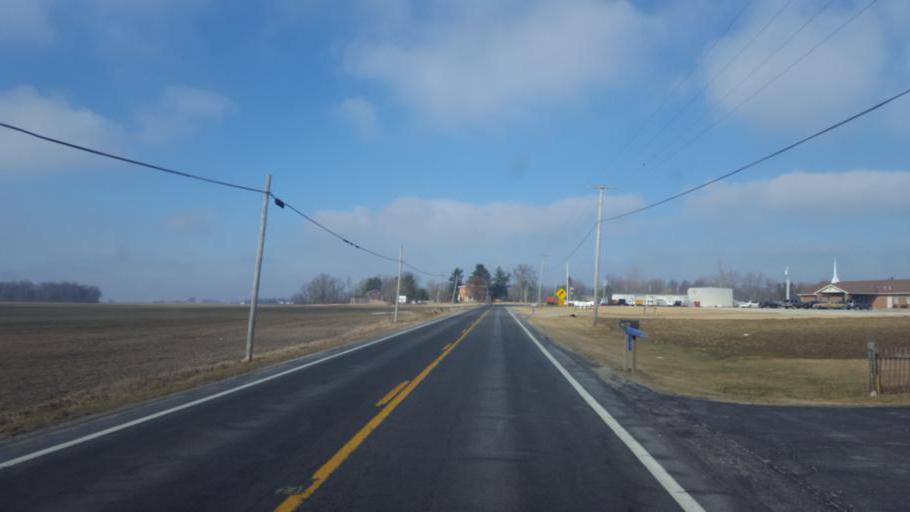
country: US
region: Ohio
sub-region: Crawford County
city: Bucyrus
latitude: 40.7817
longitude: -82.9368
